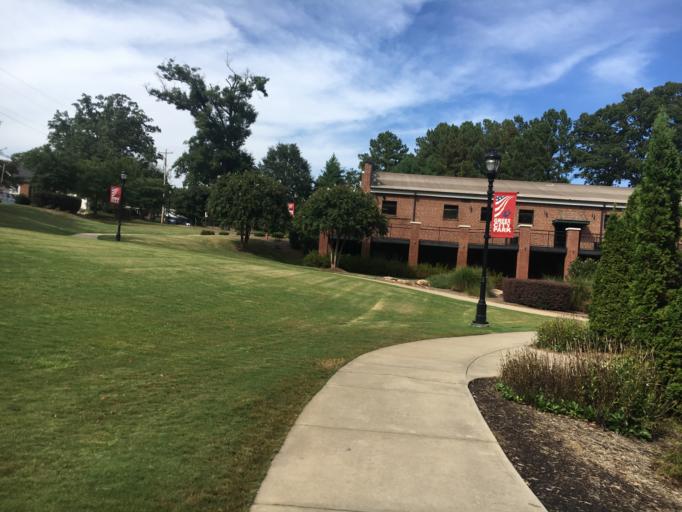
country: US
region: South Carolina
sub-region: Greenville County
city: Greer
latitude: 34.9397
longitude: -82.2235
